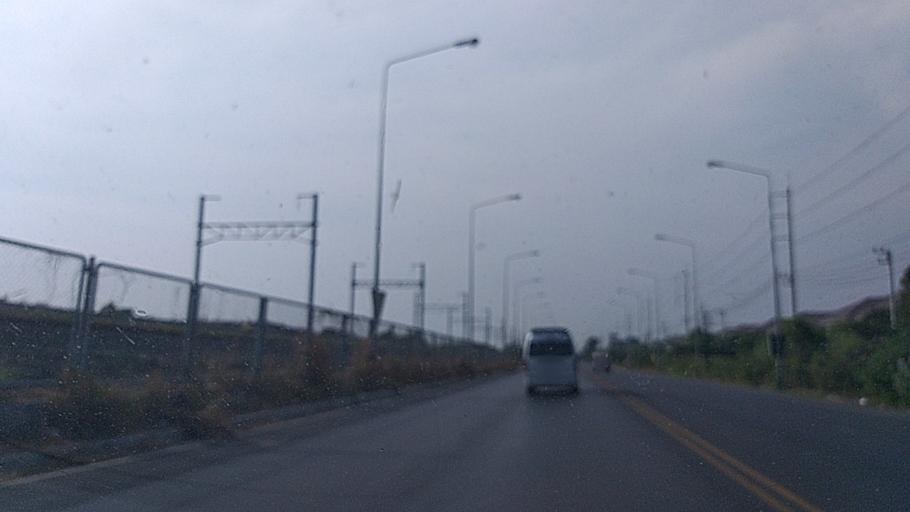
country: TH
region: Phra Nakhon Si Ayutthaya
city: Ban Bang Kadi Pathum Thani
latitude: 13.9789
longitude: 100.6035
